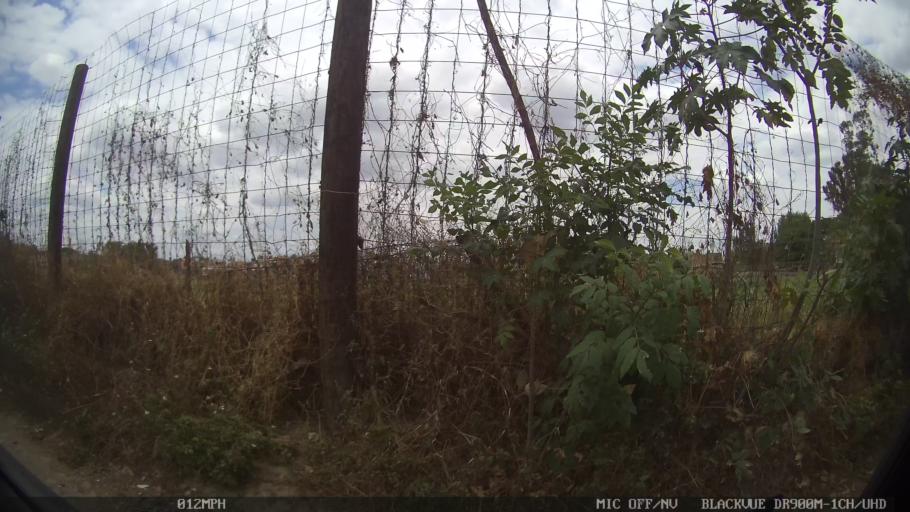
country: MX
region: Jalisco
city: Tlaquepaque
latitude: 20.6479
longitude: -103.2657
